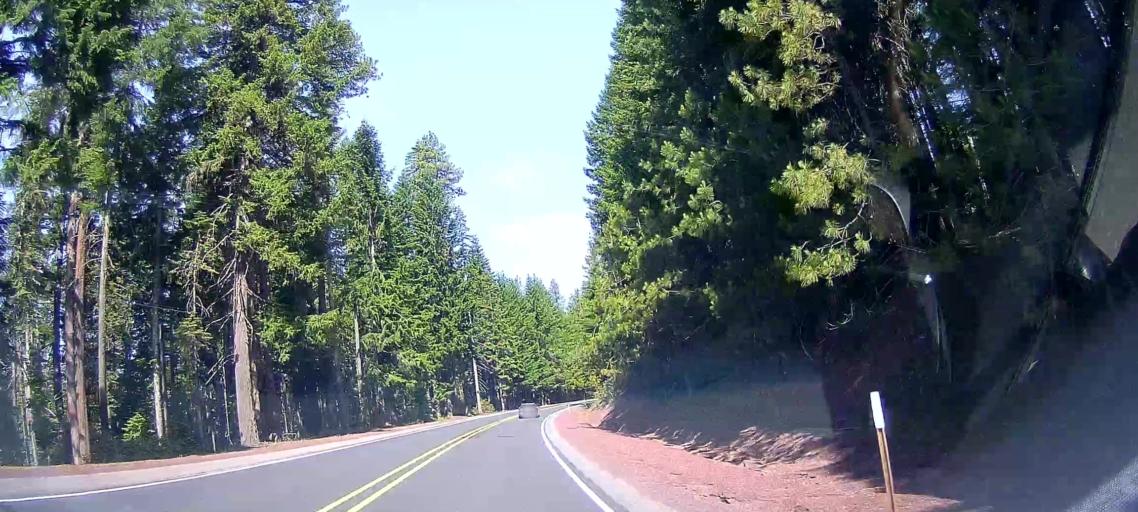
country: US
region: Oregon
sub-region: Clackamas County
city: Mount Hood Village
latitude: 45.1266
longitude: -121.5935
